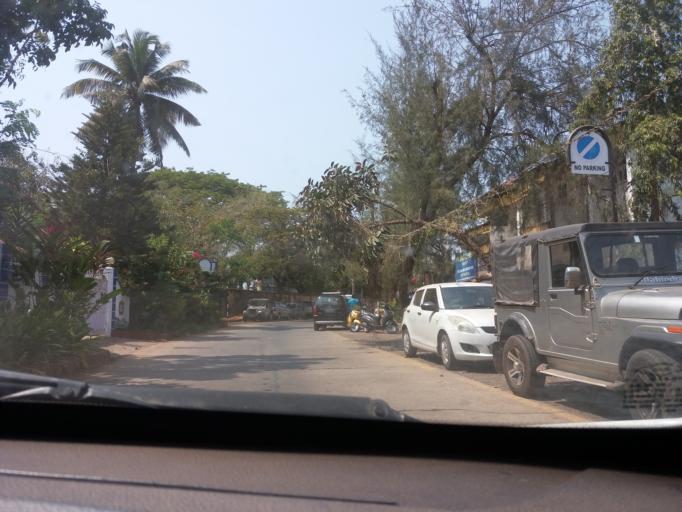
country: IN
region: Goa
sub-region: North Goa
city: Taleigao
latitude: 15.4557
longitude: 73.8031
